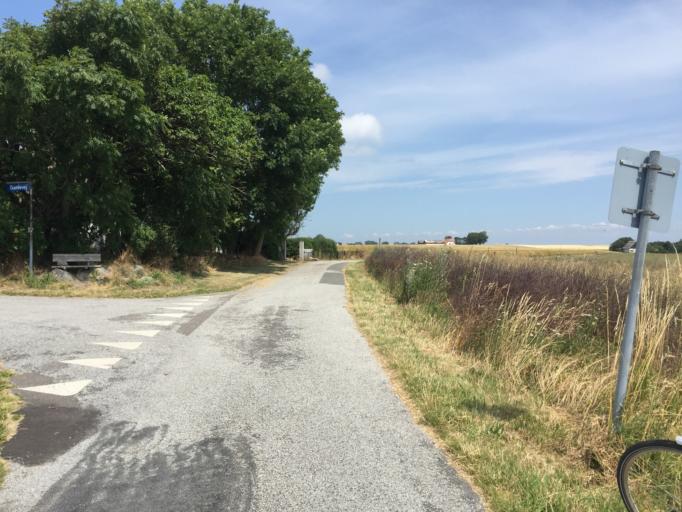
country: DK
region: Zealand
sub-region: Slagelse Kommune
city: Skaelskor
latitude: 55.1970
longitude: 11.1829
